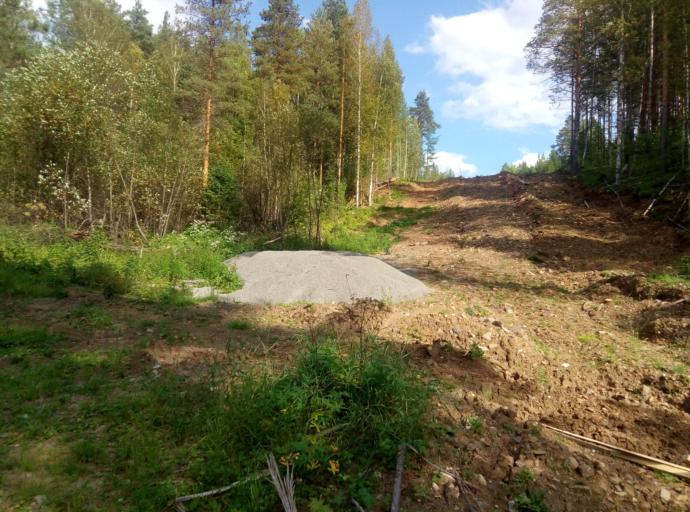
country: RU
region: Sverdlovsk
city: Krasnotur'insk
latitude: 59.6640
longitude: 60.1645
